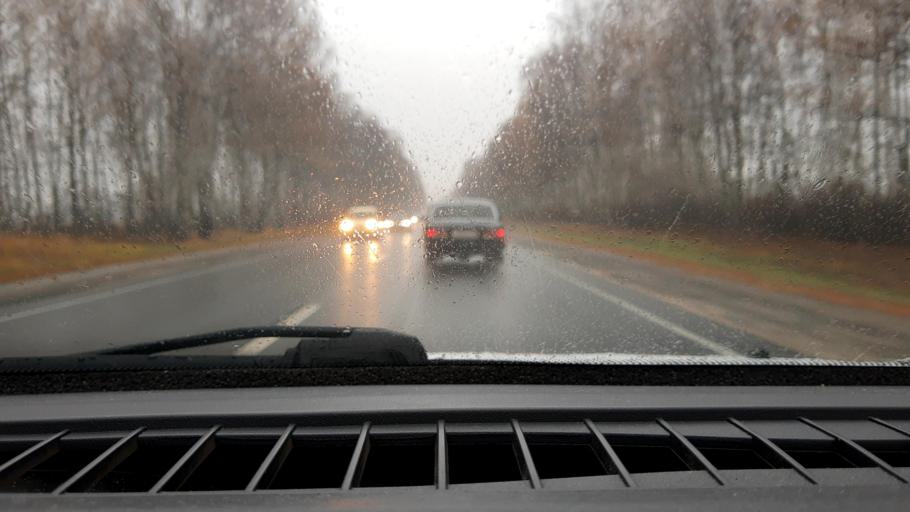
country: RU
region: Nizjnij Novgorod
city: Sitniki
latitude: 56.5162
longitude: 44.0247
